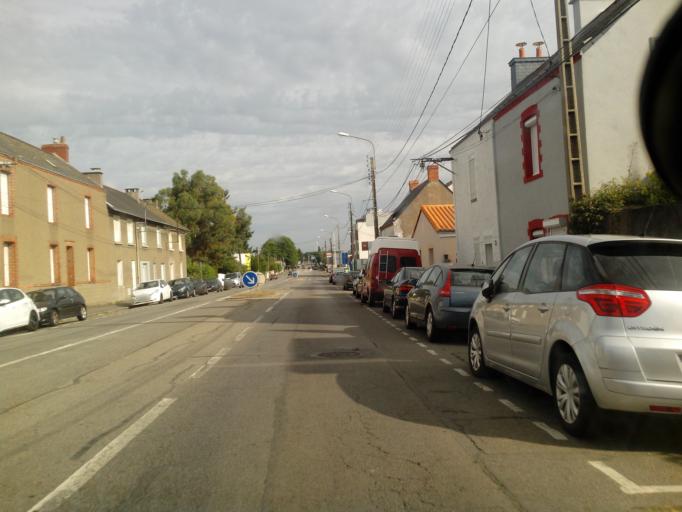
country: FR
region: Pays de la Loire
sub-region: Departement de la Loire-Atlantique
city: Orvault
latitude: 47.2566
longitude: -1.5785
